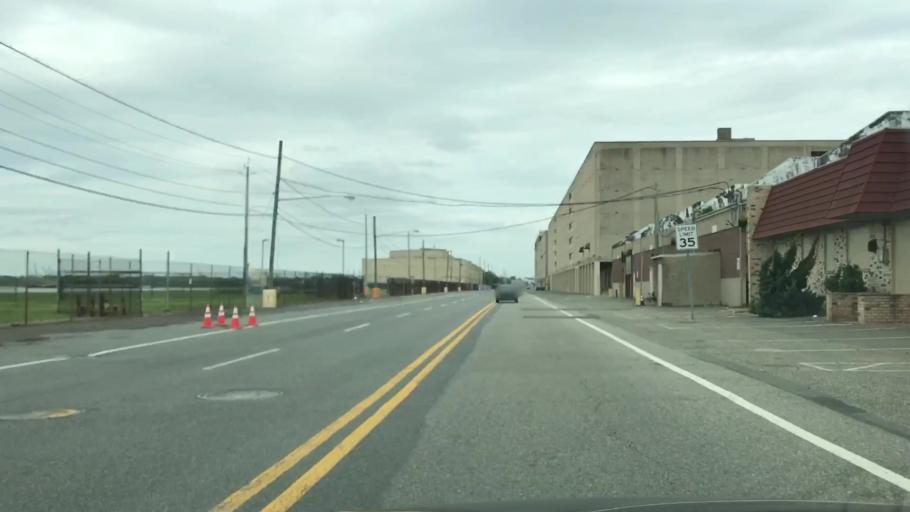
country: US
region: New Jersey
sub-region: Hudson County
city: Bayonne
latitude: 40.6649
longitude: -74.0790
